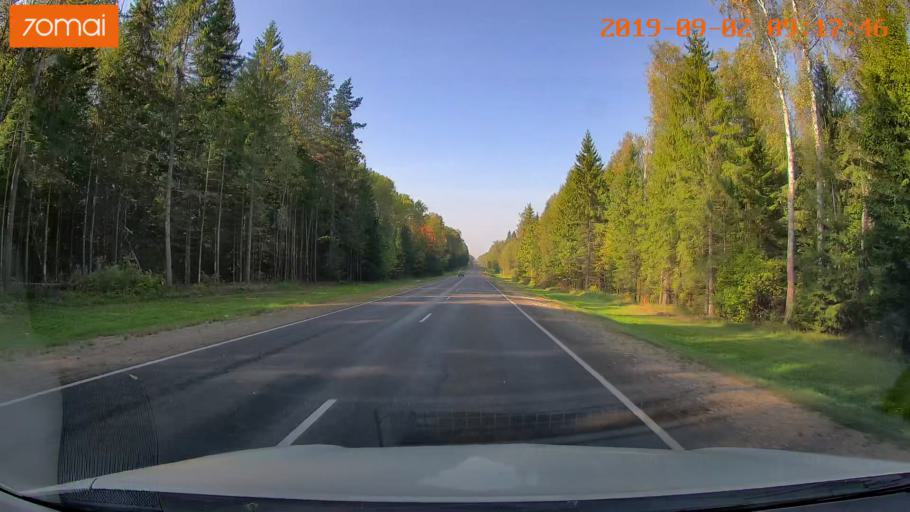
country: RU
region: Kaluga
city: Nikola-Lenivets
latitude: 54.8216
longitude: 35.4441
